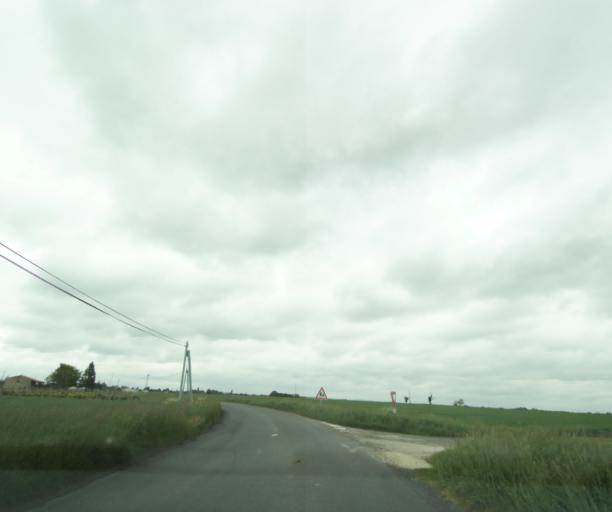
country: FR
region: Poitou-Charentes
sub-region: Departement de la Charente-Maritime
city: Chaniers
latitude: 45.7047
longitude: -0.5640
